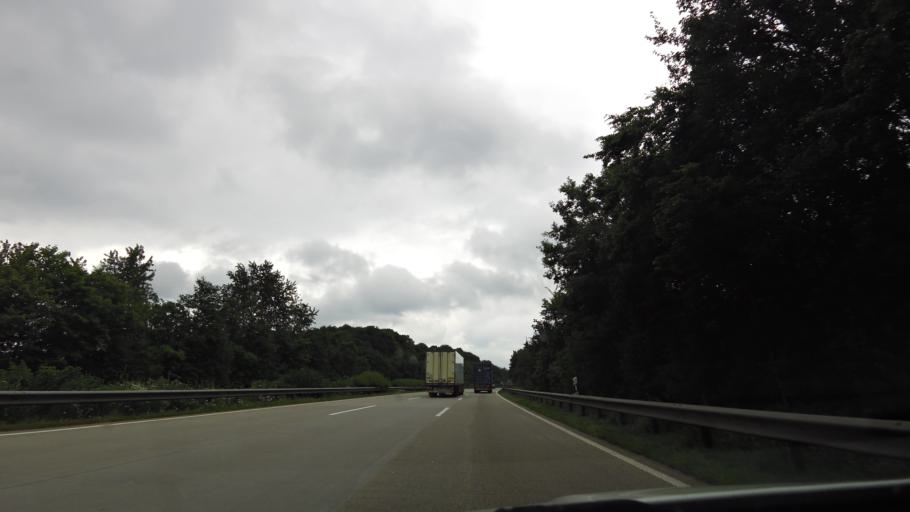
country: DE
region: Rheinland-Pfalz
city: Waldorf
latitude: 50.4977
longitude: 7.2249
